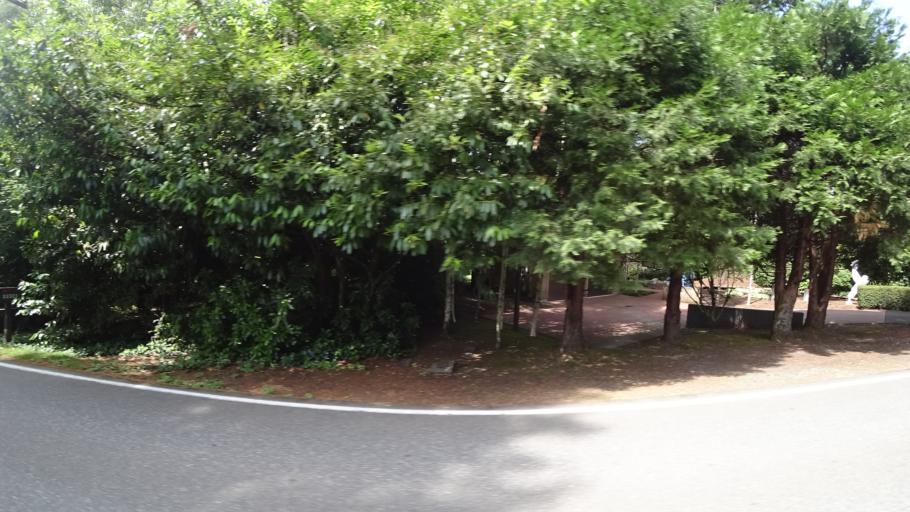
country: US
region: Oregon
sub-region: Clackamas County
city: Lake Oswego
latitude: 45.4425
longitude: -122.6675
